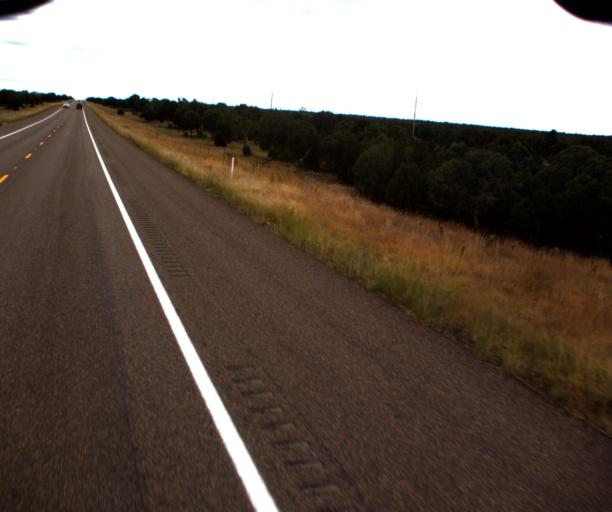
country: US
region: Arizona
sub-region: Navajo County
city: White Mountain Lake
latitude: 34.3224
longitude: -110.0437
